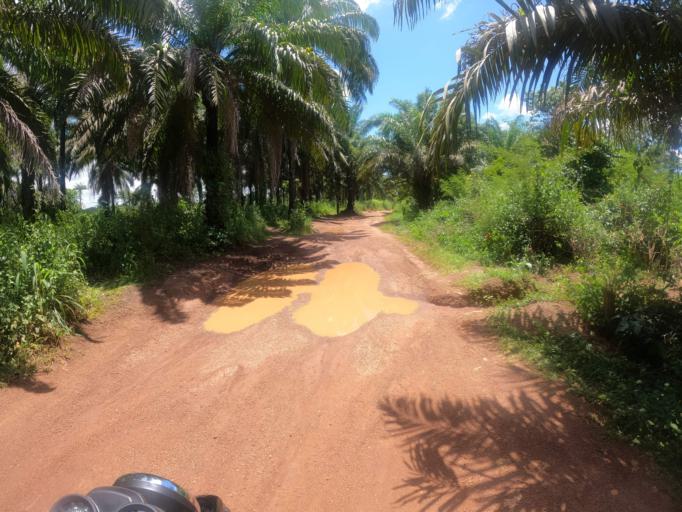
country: SL
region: Northern Province
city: Makeni
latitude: 8.8684
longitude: -12.1050
